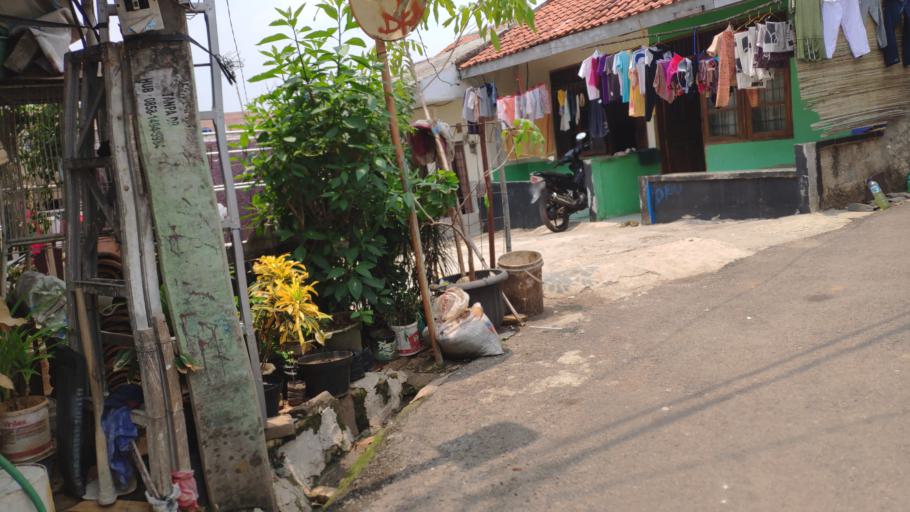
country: ID
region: West Java
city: Depok
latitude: -6.3492
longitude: 106.8046
